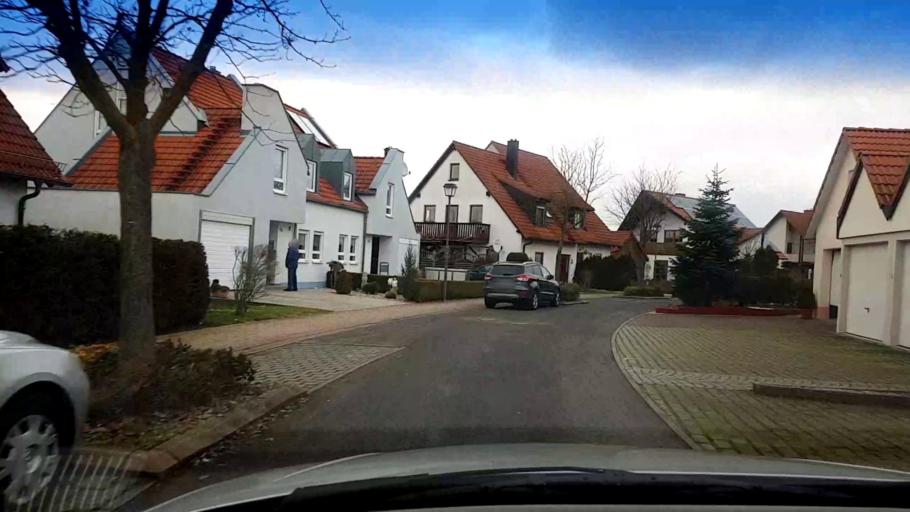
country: DE
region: Bavaria
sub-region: Upper Franconia
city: Baunach
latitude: 49.9801
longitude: 10.8480
